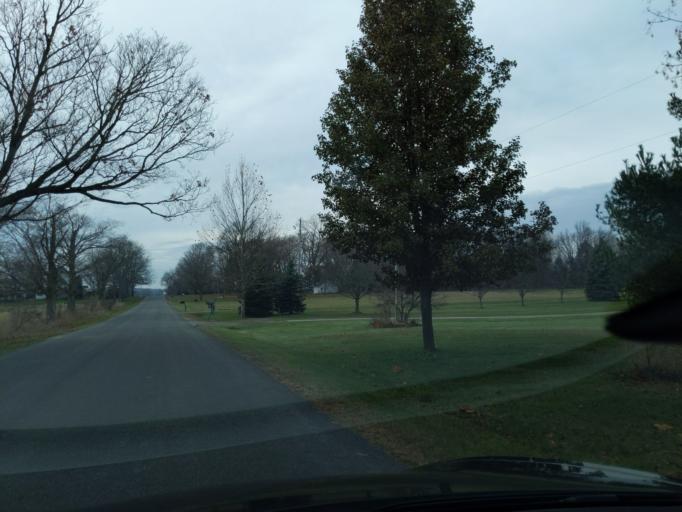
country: US
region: Michigan
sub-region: Ingham County
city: Okemos
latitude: 42.6544
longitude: -84.3717
